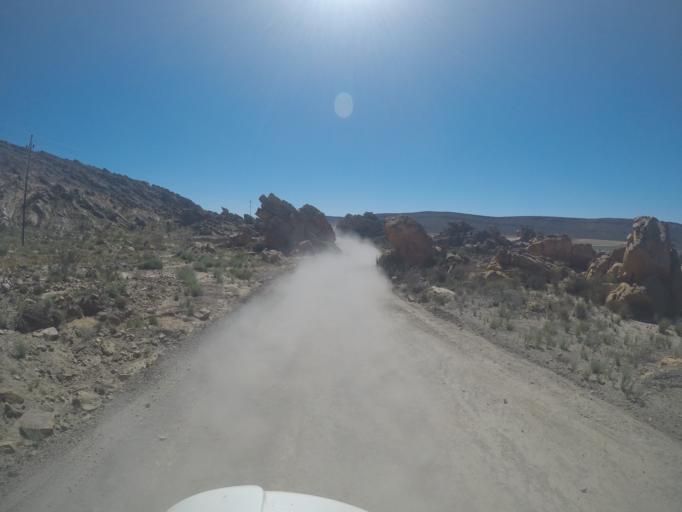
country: ZA
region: Western Cape
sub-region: Cape Winelands District Municipality
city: Ceres
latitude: -32.8479
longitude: 19.4460
